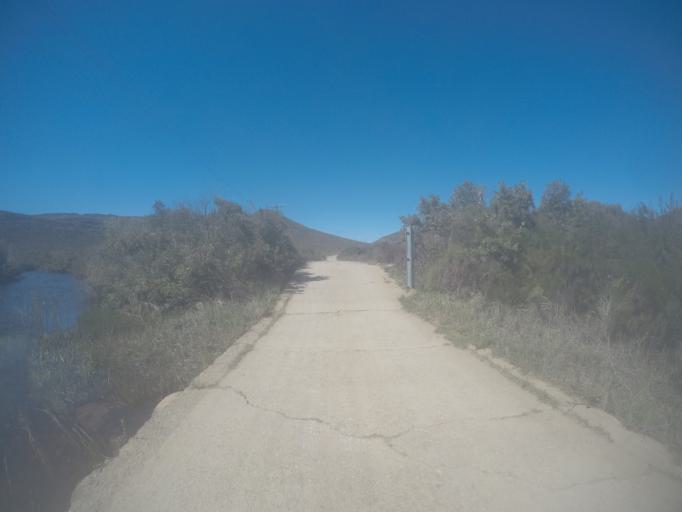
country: ZA
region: Western Cape
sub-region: West Coast District Municipality
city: Clanwilliam
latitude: -32.5188
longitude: 19.3505
